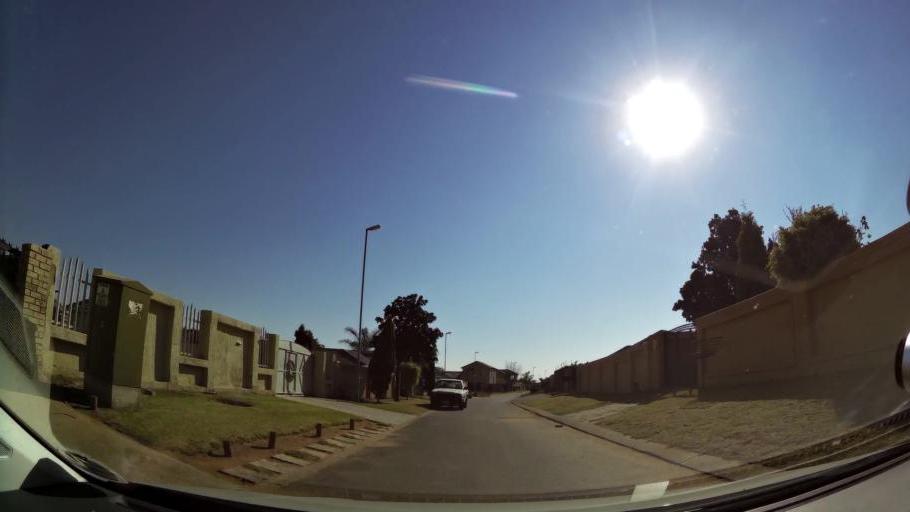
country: ZA
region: Gauteng
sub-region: City of Johannesburg Metropolitan Municipality
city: Modderfontein
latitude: -26.0468
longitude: 28.2009
